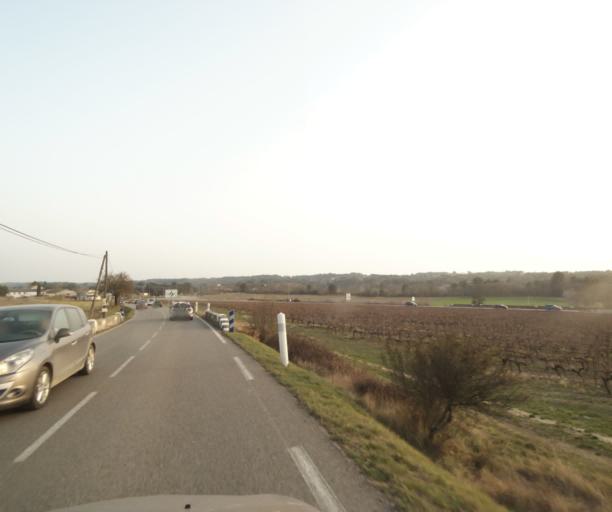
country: FR
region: Provence-Alpes-Cote d'Azur
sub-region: Departement des Bouches-du-Rhone
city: Eguilles
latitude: 43.5889
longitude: 5.3677
